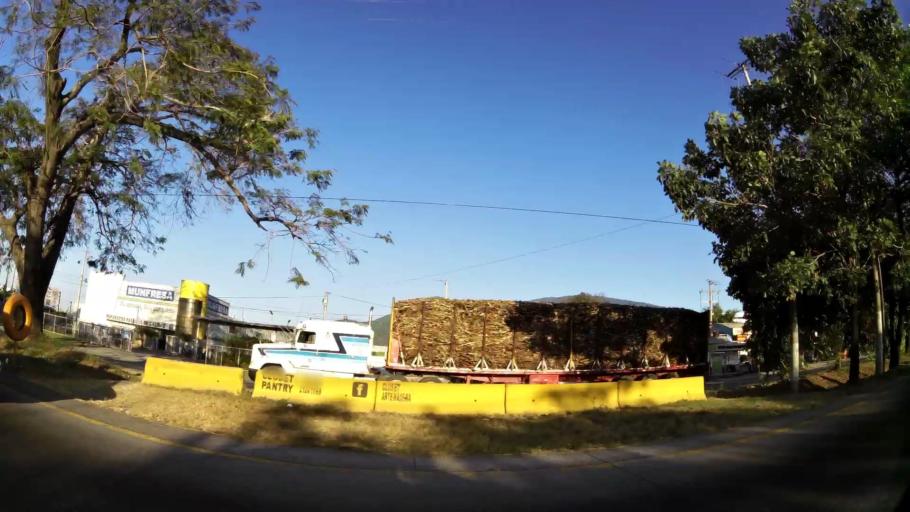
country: SV
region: La Libertad
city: Santa Tecla
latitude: 13.7430
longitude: -89.3632
